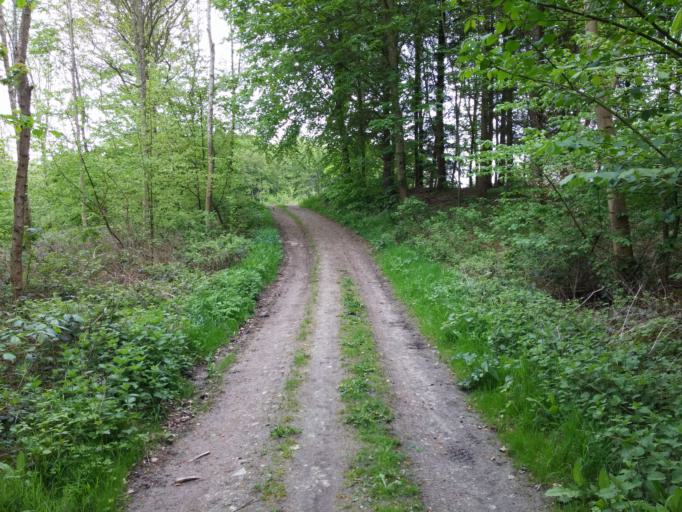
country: DK
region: South Denmark
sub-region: Kerteminde Kommune
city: Munkebo
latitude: 55.4276
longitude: 10.5638
